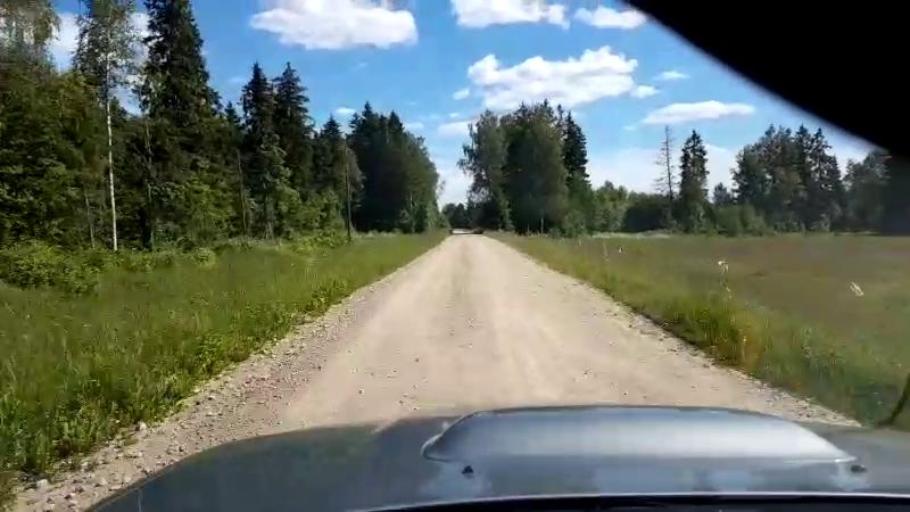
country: EE
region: Paernumaa
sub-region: Halinga vald
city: Parnu-Jaagupi
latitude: 58.5335
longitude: 24.5464
